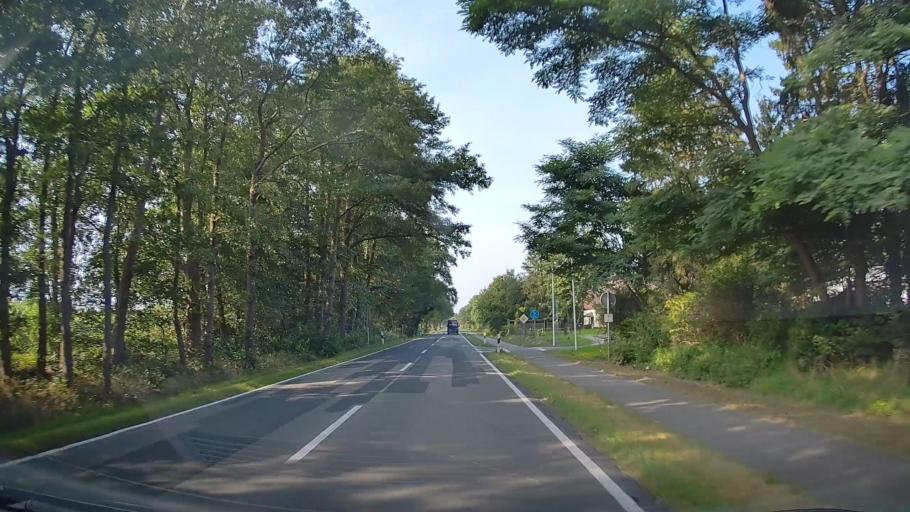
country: DE
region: Lower Saxony
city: Friesoythe
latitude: 53.1029
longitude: 7.8319
